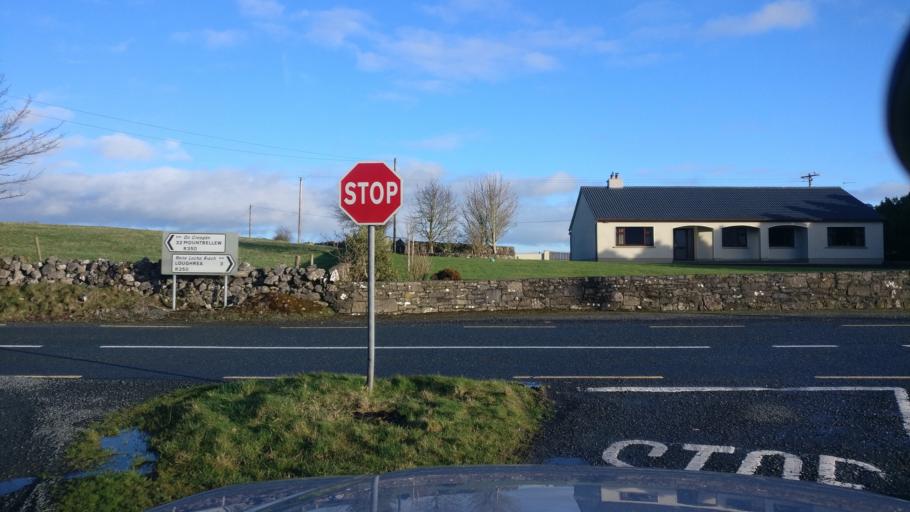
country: IE
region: Connaught
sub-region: County Galway
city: Loughrea
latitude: 53.2281
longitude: -8.5594
